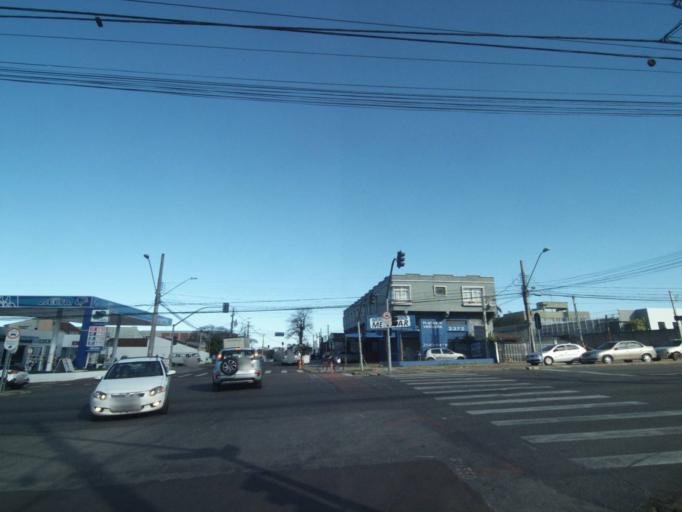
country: BR
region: Parana
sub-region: Curitiba
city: Curitiba
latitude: -25.3938
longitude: -49.2410
